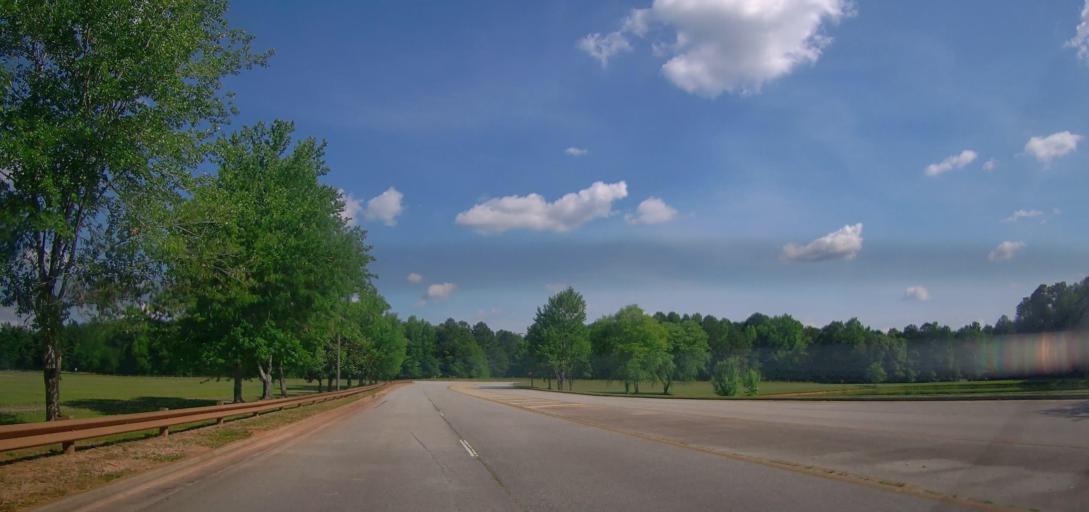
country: US
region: Georgia
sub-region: Henry County
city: Hampton
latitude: 33.3800
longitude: -84.3238
